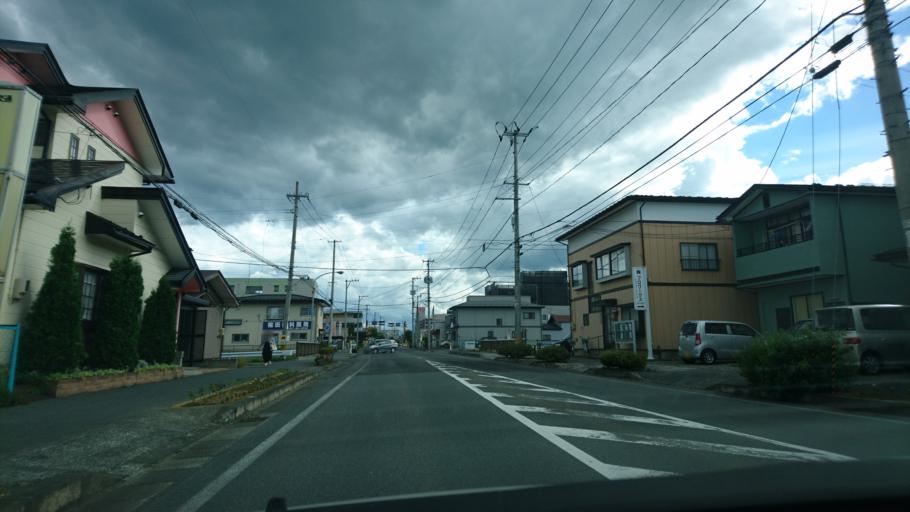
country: JP
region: Iwate
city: Kitakami
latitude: 39.2938
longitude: 141.1204
